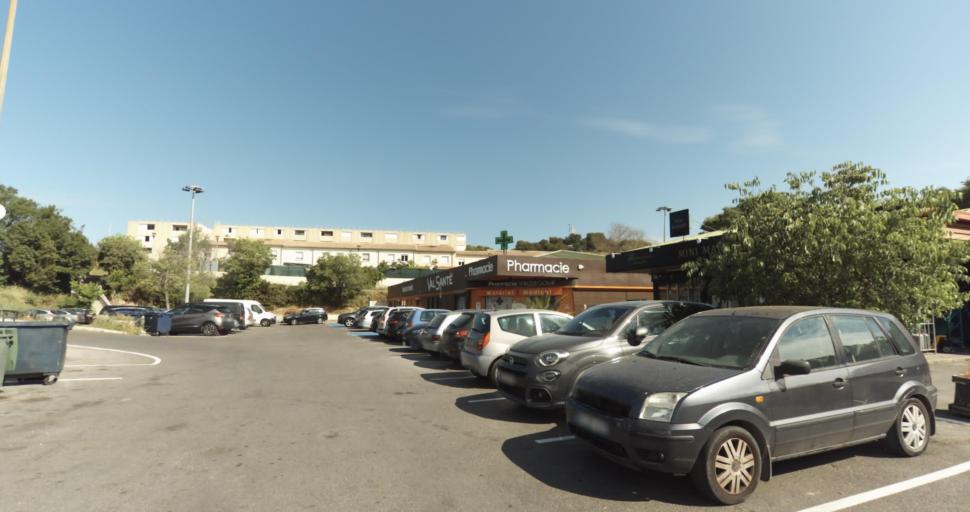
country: FR
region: Languedoc-Roussillon
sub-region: Departement du Gard
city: Nimes
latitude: 43.8311
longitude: 4.3287
